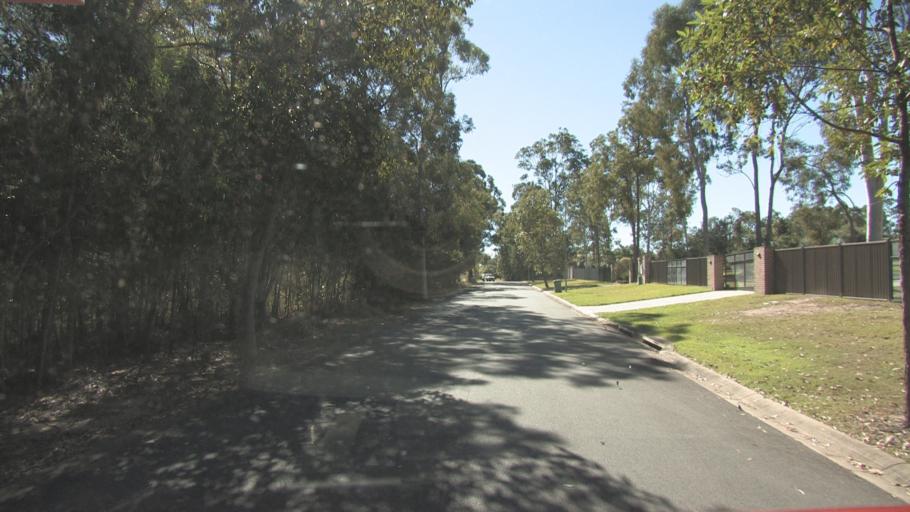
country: AU
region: Queensland
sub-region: Logan
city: Park Ridge South
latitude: -27.7134
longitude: 153.0450
